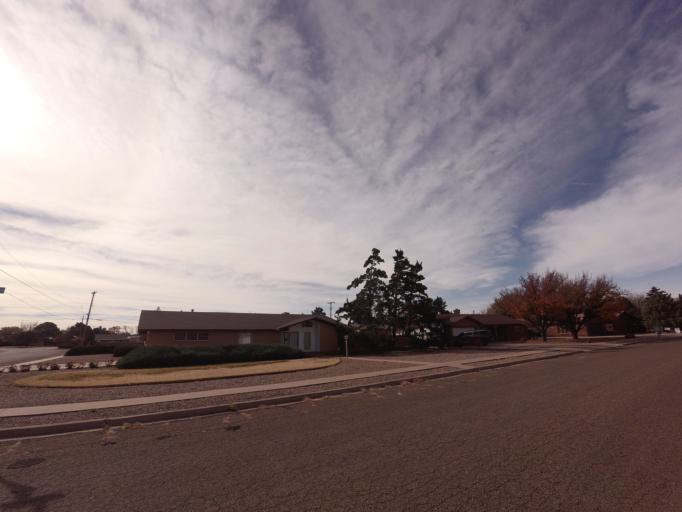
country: US
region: New Mexico
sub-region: Curry County
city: Clovis
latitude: 34.4182
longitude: -103.1912
